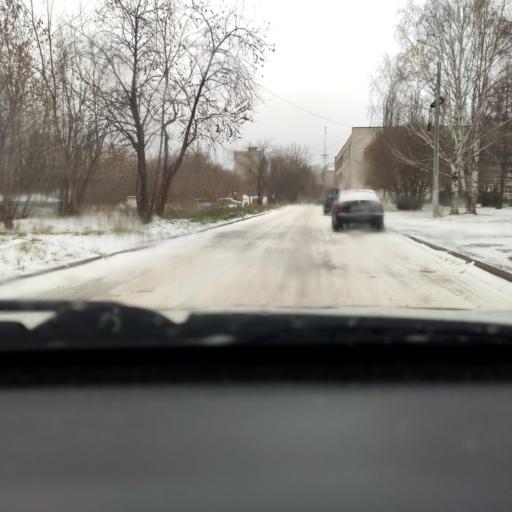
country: RU
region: Perm
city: Perm
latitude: 58.0131
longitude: 56.2790
